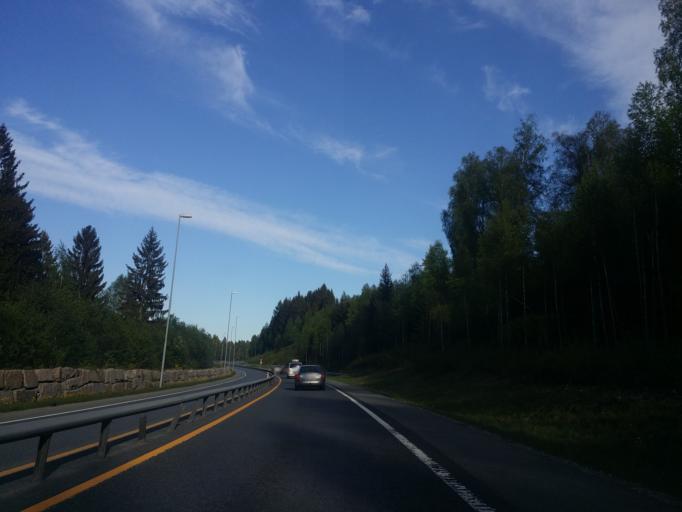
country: NO
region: Buskerud
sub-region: Drammen
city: Drammen
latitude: 59.7407
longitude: 10.1385
